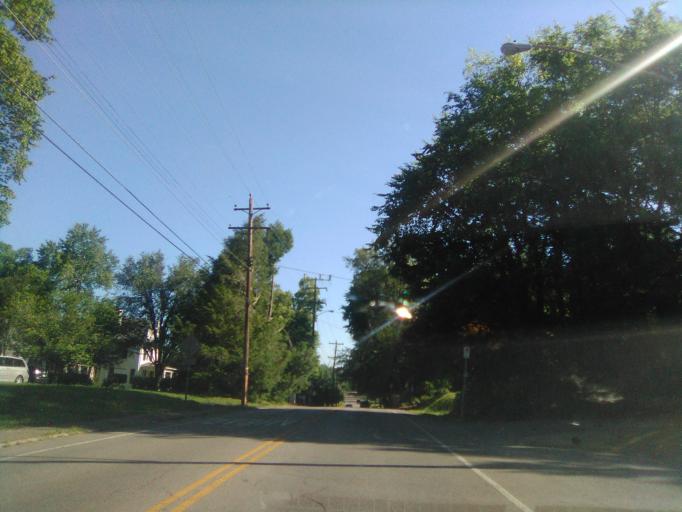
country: US
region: Tennessee
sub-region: Davidson County
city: Belle Meade
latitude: 36.1190
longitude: -86.8360
